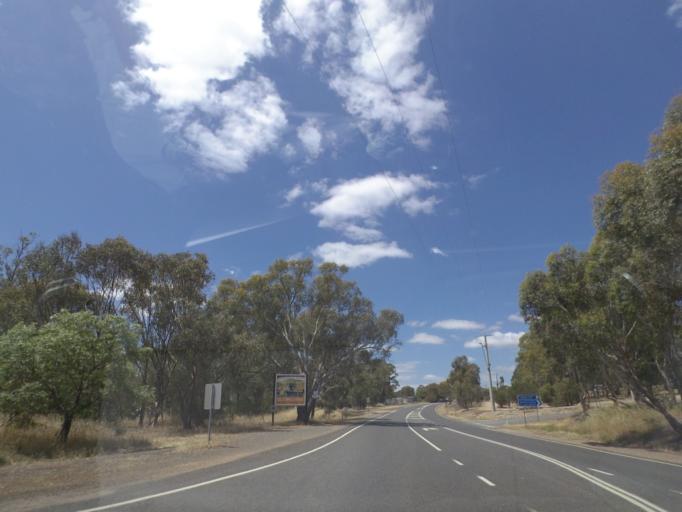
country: AU
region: Victoria
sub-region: Wangaratta
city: Wangaratta
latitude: -36.4643
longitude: 146.2167
